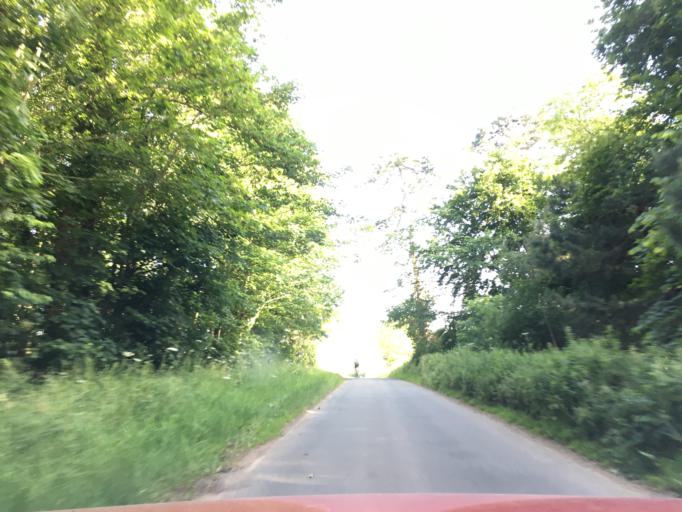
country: GB
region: England
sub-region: Gloucestershire
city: Lechlade
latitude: 51.7571
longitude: -1.7218
